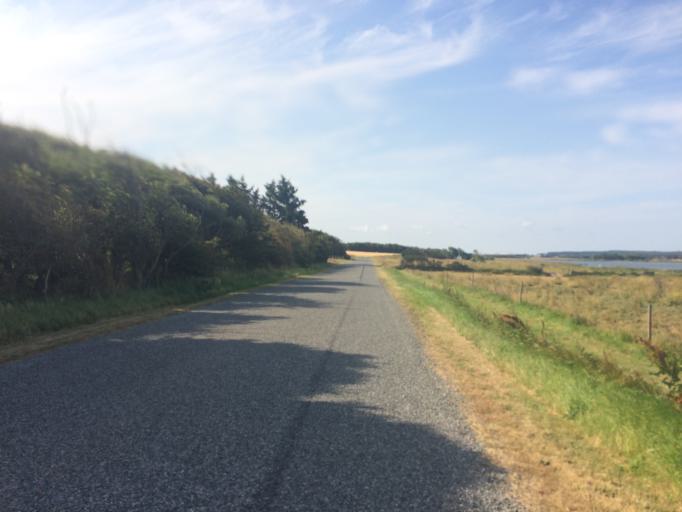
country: DK
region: North Denmark
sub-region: Morso Kommune
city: Nykobing Mors
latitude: 56.6491
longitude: 8.7843
